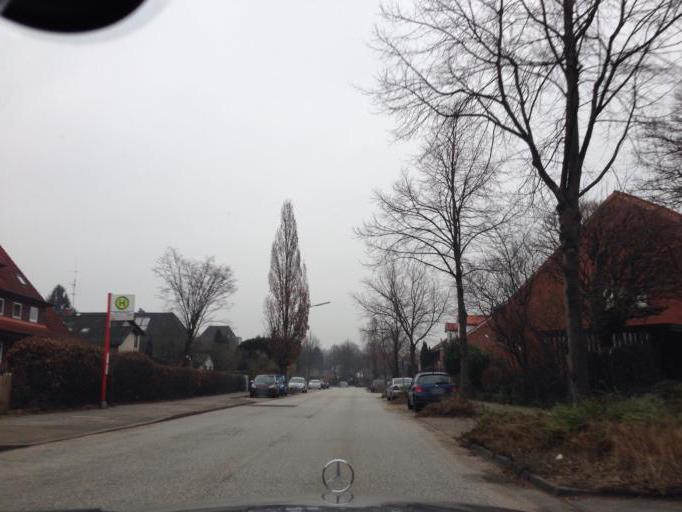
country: DE
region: Hamburg
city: Farmsen-Berne
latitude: 53.6018
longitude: 10.1082
